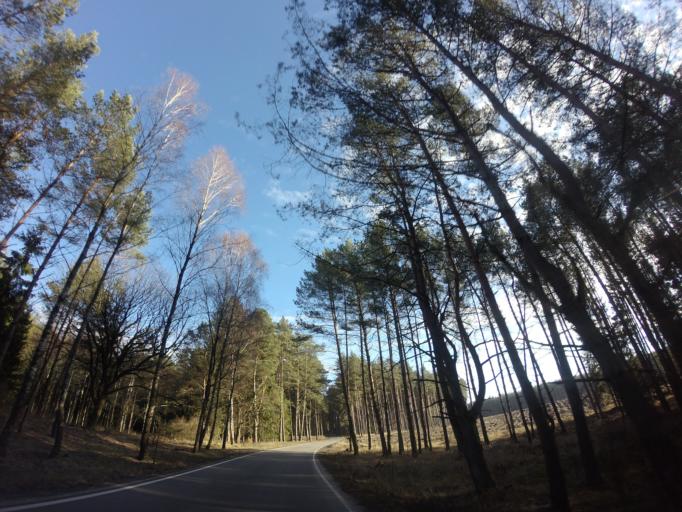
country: PL
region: West Pomeranian Voivodeship
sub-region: Powiat choszczenski
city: Drawno
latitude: 53.1268
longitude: 15.7290
